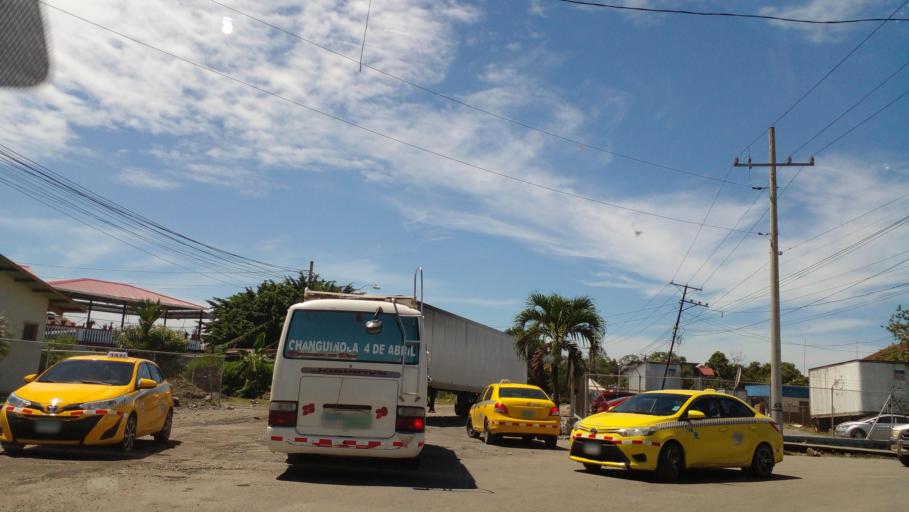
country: PA
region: Bocas del Toro
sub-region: Distrito de Changuinola
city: Changuinola
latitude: 9.4717
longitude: -82.5172
